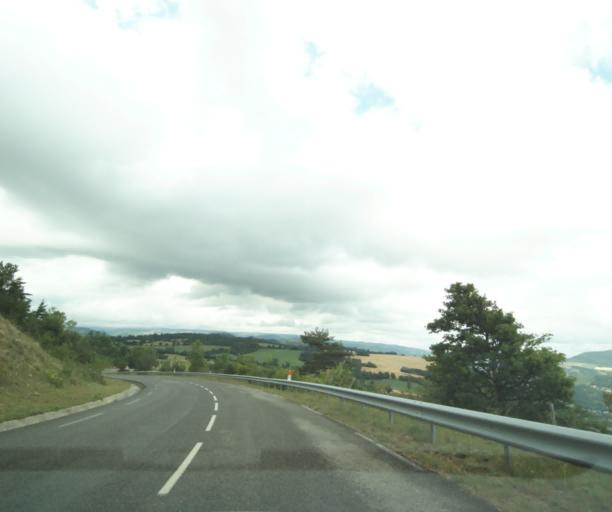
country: FR
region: Languedoc-Roussillon
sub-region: Departement de la Lozere
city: La Canourgue
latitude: 44.4202
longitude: 3.1815
